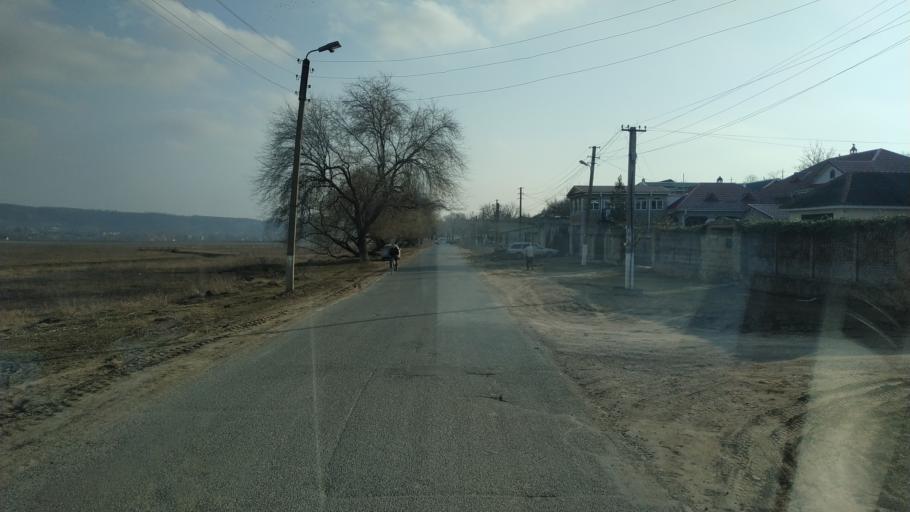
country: MD
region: Hincesti
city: Dancu
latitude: 46.7739
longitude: 28.3462
